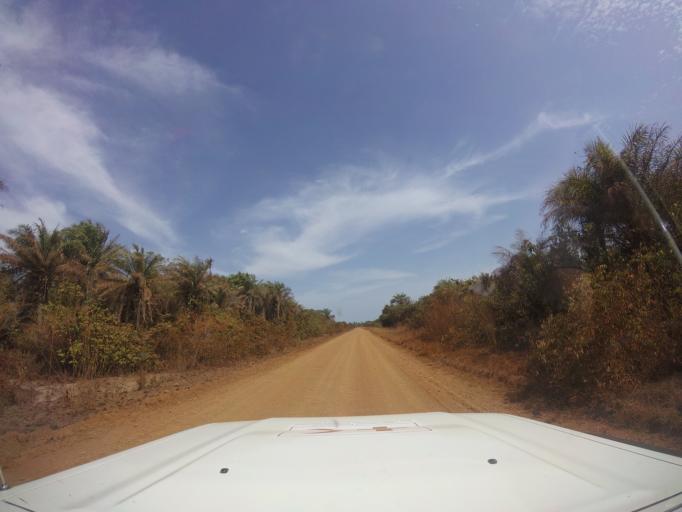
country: LR
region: Grand Cape Mount
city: Robertsport
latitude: 6.6963
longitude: -11.2848
